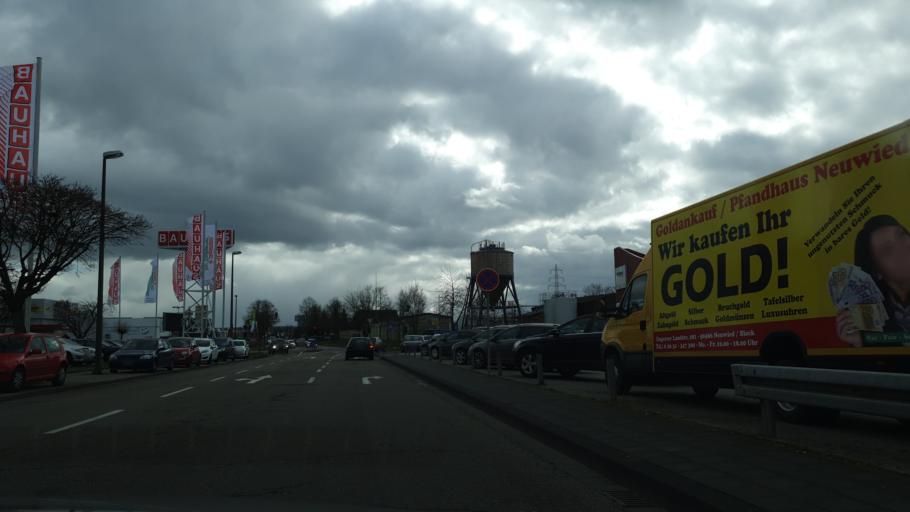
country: DE
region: Rheinland-Pfalz
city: Neuwied
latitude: 50.4388
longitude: 7.4888
